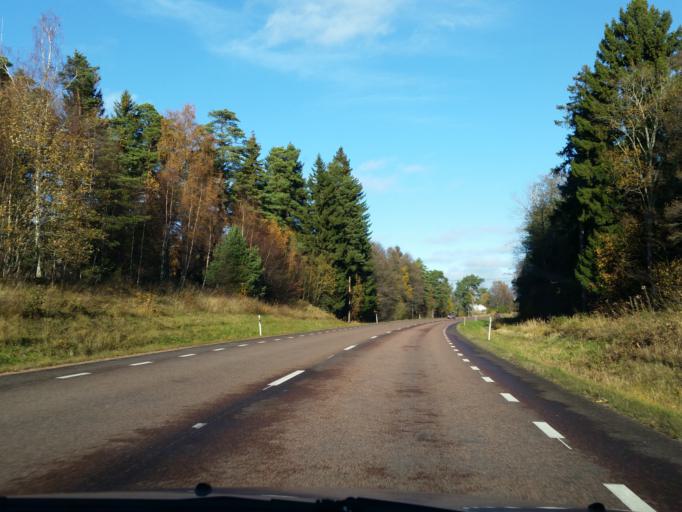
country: AX
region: Alands landsbygd
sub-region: Finstroem
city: Finstroem
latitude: 60.2233
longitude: 19.9840
